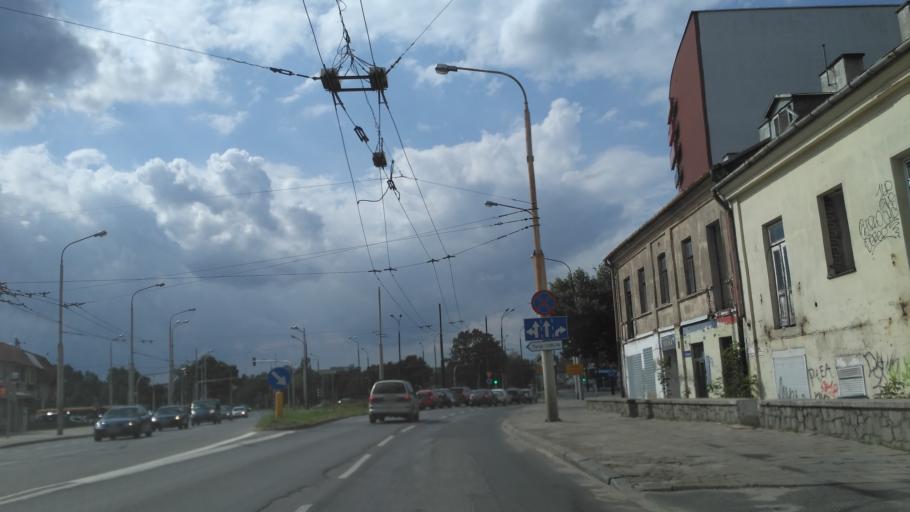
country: PL
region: Lublin Voivodeship
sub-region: Powiat lubelski
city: Lublin
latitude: 51.2377
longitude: 22.5736
